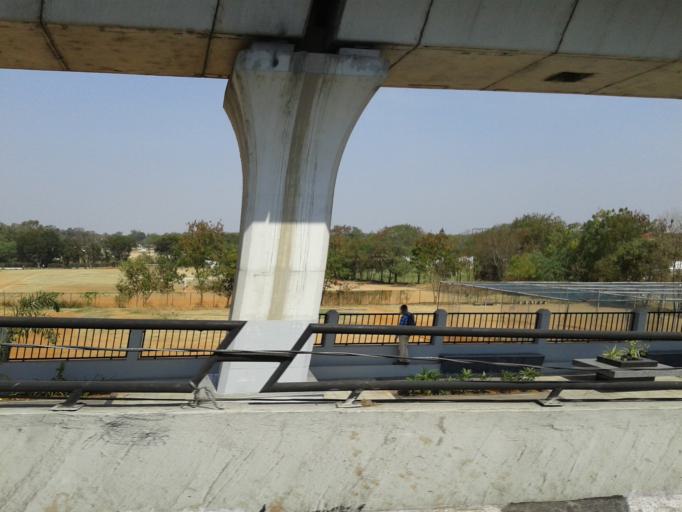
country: IN
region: Telangana
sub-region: Hyderabad
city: Malkajgiri
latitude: 17.4433
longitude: 78.4890
